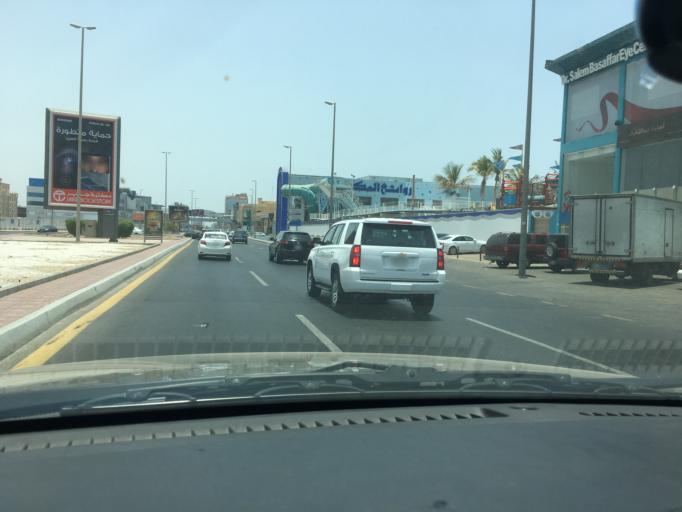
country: SA
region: Makkah
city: Jeddah
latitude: 21.5942
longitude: 39.1440
